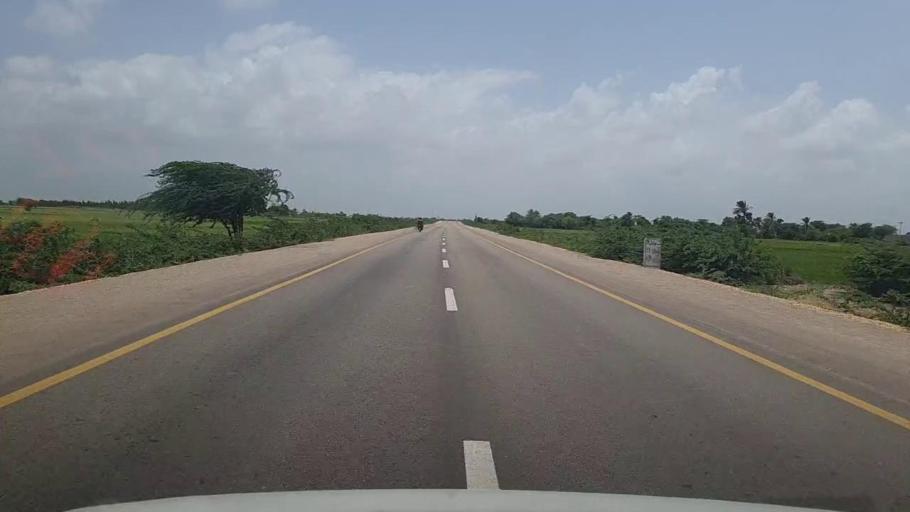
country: PK
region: Sindh
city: Thatta
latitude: 24.7663
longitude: 67.9456
